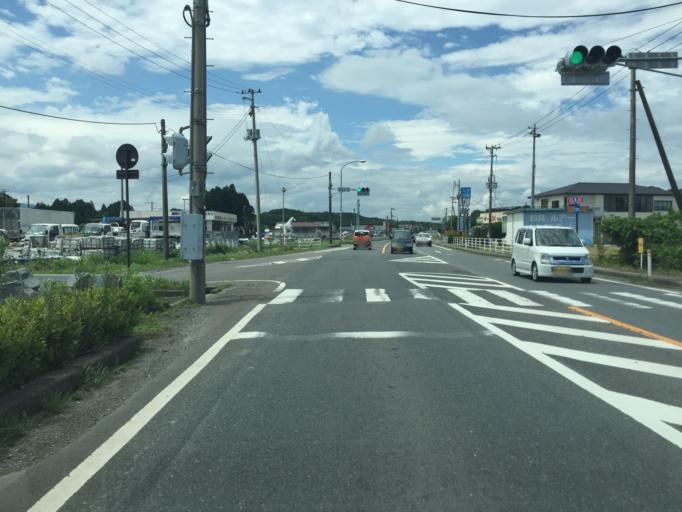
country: JP
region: Fukushima
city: Namie
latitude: 37.7170
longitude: 140.9587
